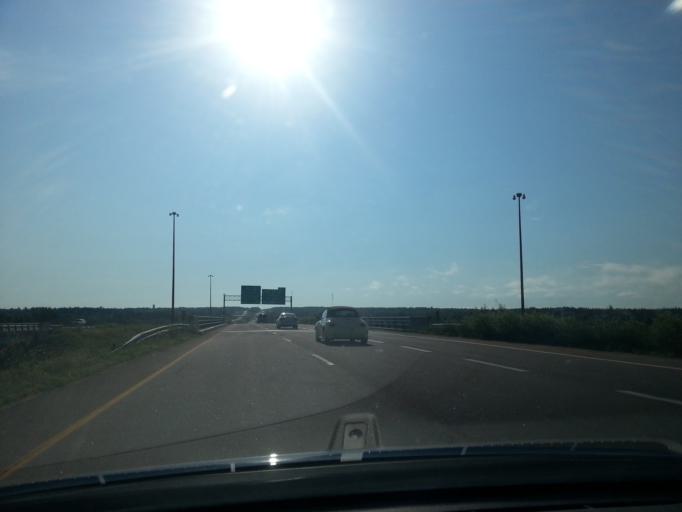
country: CA
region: New Brunswick
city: Shediac
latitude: 46.2094
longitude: -64.5680
